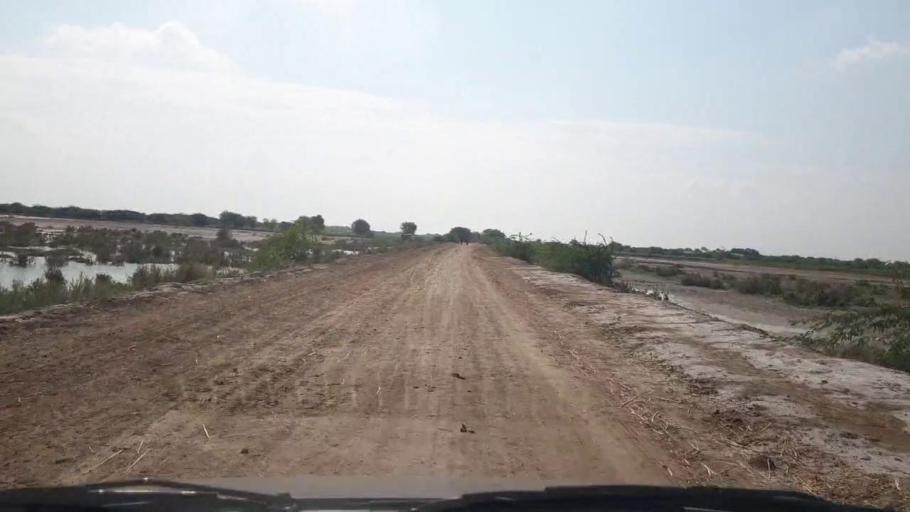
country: PK
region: Sindh
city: Badin
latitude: 24.4888
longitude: 68.6121
